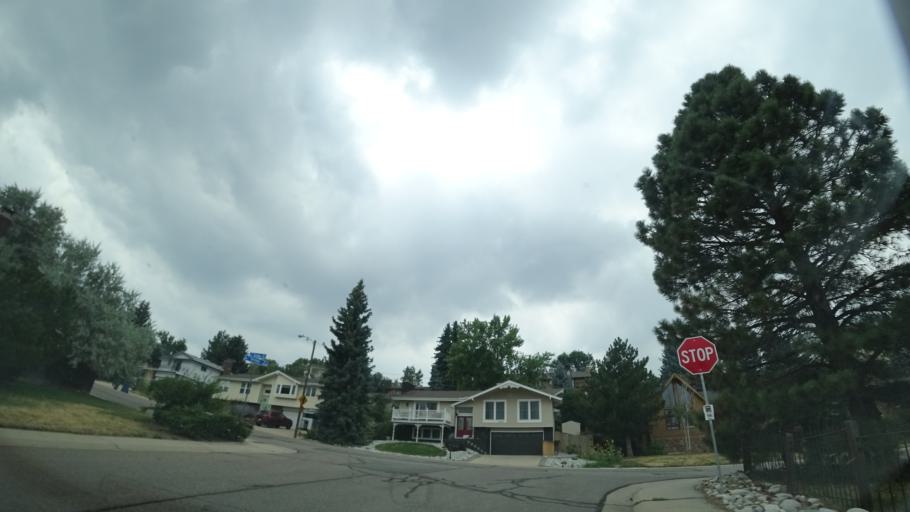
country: US
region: Colorado
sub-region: Jefferson County
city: West Pleasant View
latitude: 39.7071
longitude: -105.1557
